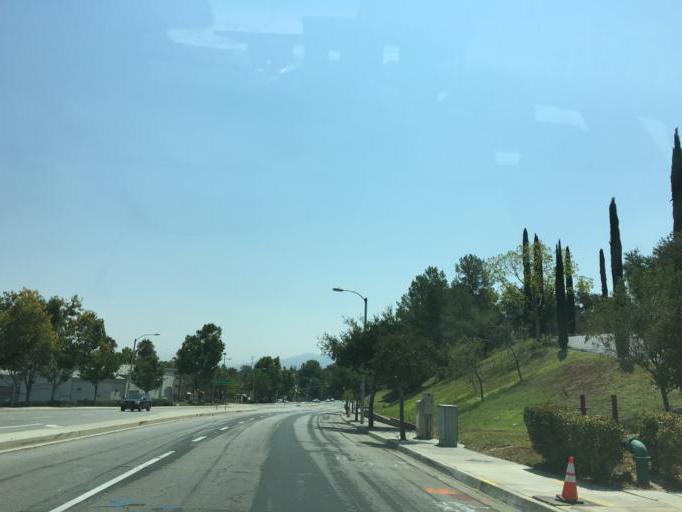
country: US
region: California
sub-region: Los Angeles County
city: Santa Clarita
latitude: 34.3817
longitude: -118.5738
